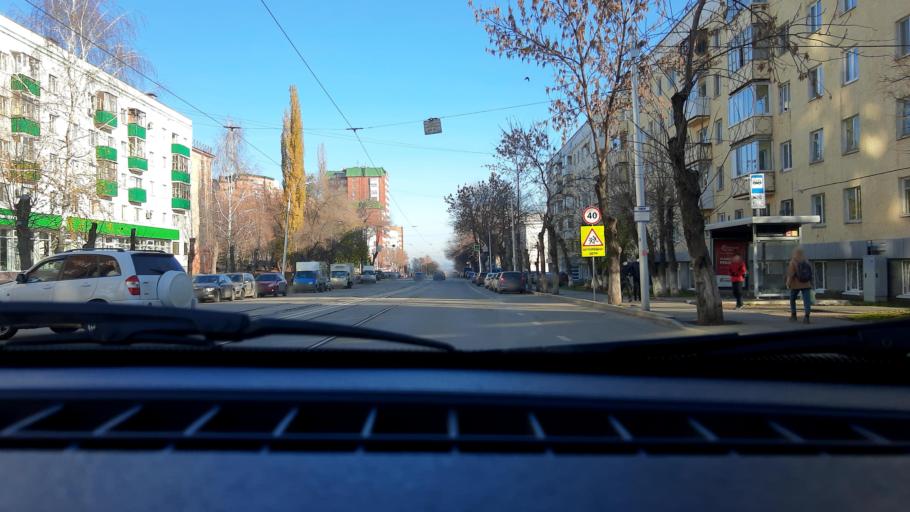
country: RU
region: Bashkortostan
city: Ufa
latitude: 54.7433
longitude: 55.9572
